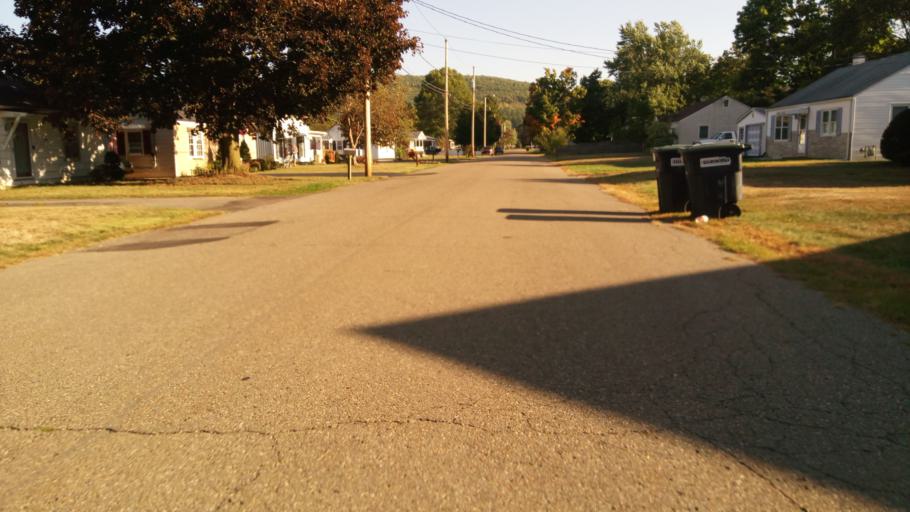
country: US
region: New York
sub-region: Chemung County
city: Southport
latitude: 42.0590
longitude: -76.8239
